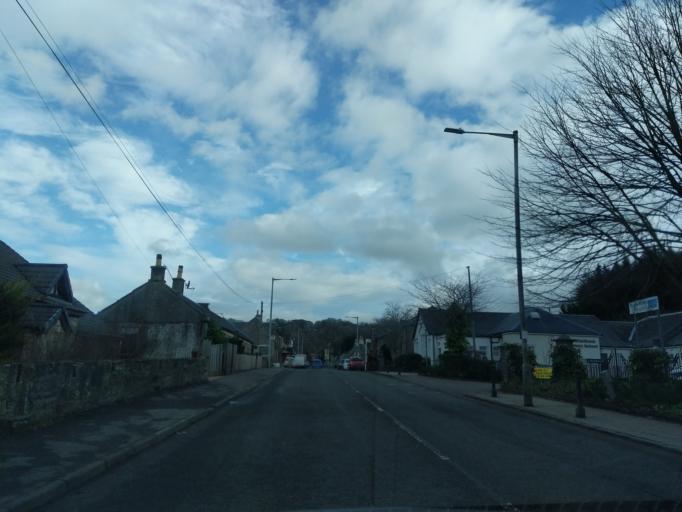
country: GB
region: Scotland
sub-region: South Lanarkshire
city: Lanark
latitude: 55.6746
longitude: -3.8090
